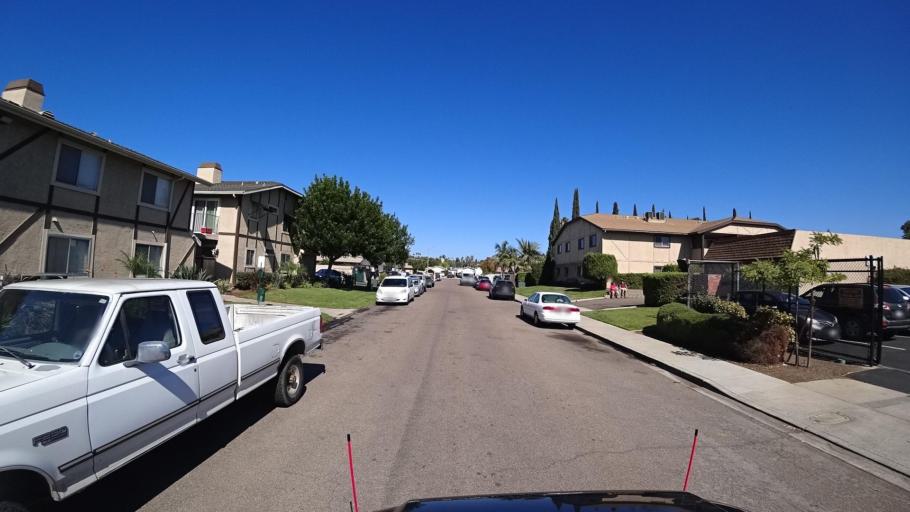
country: US
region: California
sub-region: San Diego County
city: Winter Gardens
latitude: 32.8214
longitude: -116.9319
